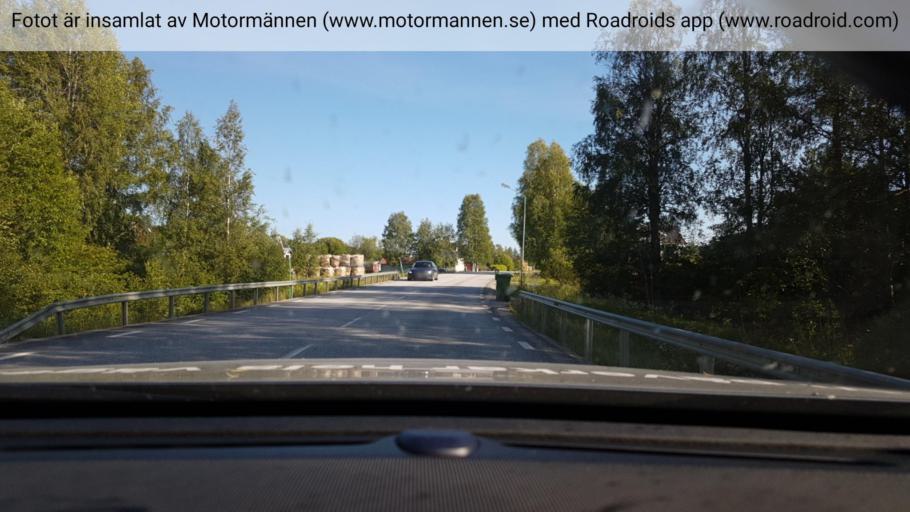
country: SE
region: Vaesterbotten
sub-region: Vindelns Kommun
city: Vindeln
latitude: 64.1660
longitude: 19.4971
